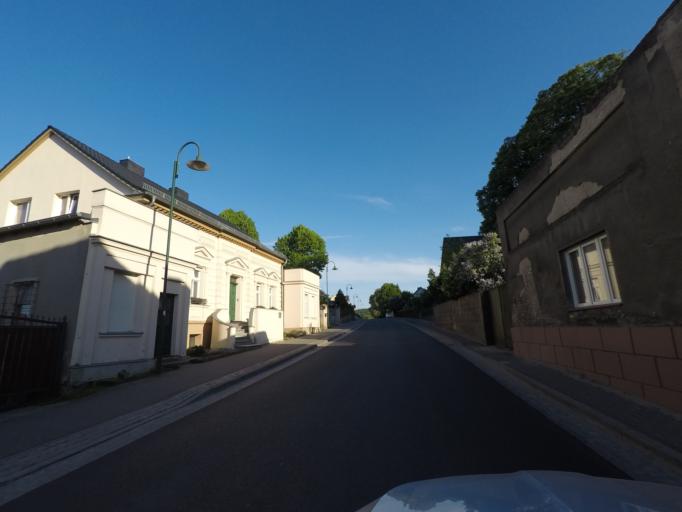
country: DE
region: Brandenburg
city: Falkenberg
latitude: 52.8038
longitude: 13.9590
